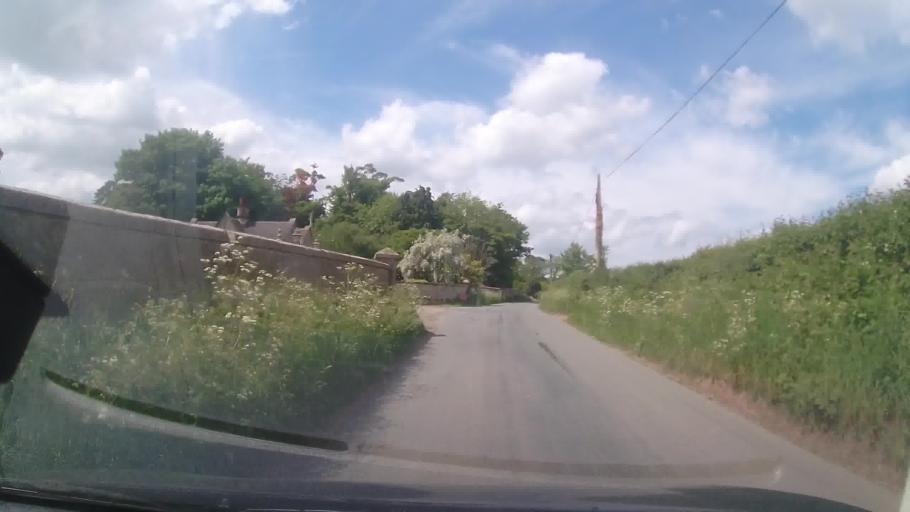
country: GB
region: England
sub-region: Shropshire
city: Clive
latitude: 52.8066
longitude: -2.6859
